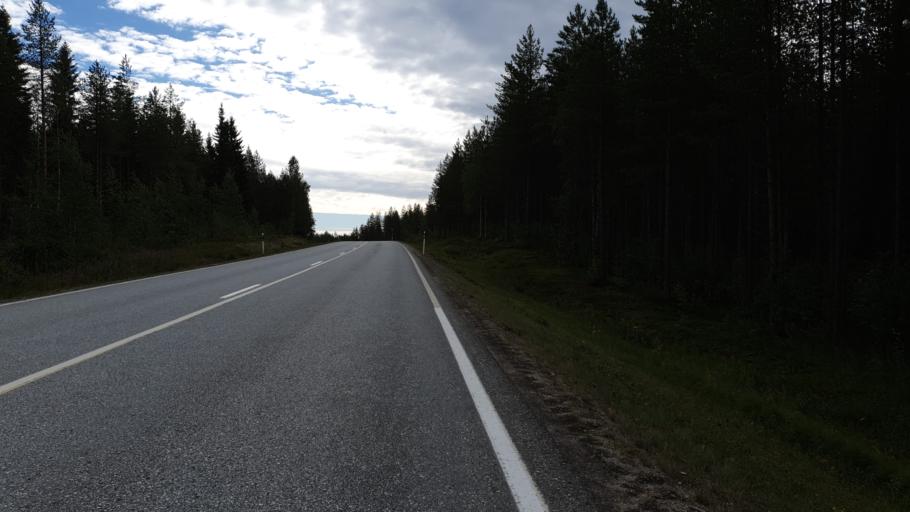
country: FI
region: Kainuu
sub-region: Kehys-Kainuu
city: Kuhmo
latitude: 64.4799
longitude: 29.7572
